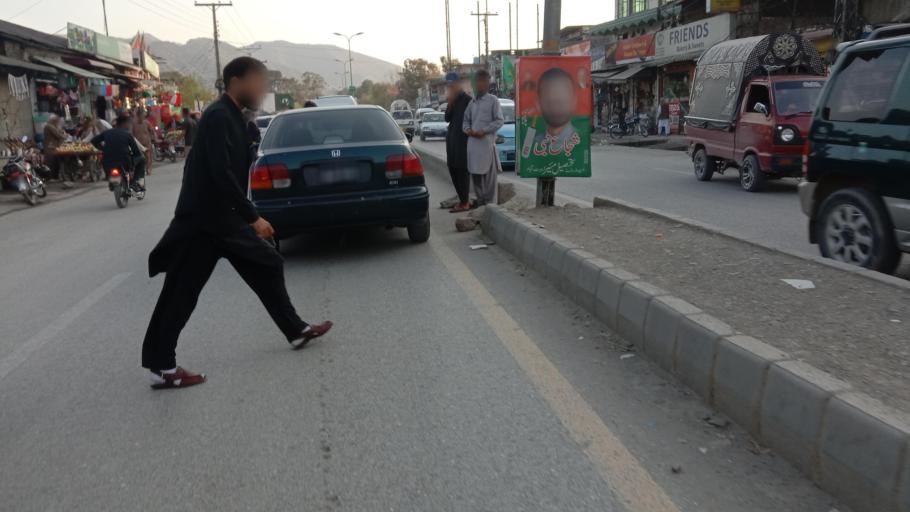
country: PK
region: Khyber Pakhtunkhwa
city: Abbottabad
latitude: 34.1684
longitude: 73.2246
